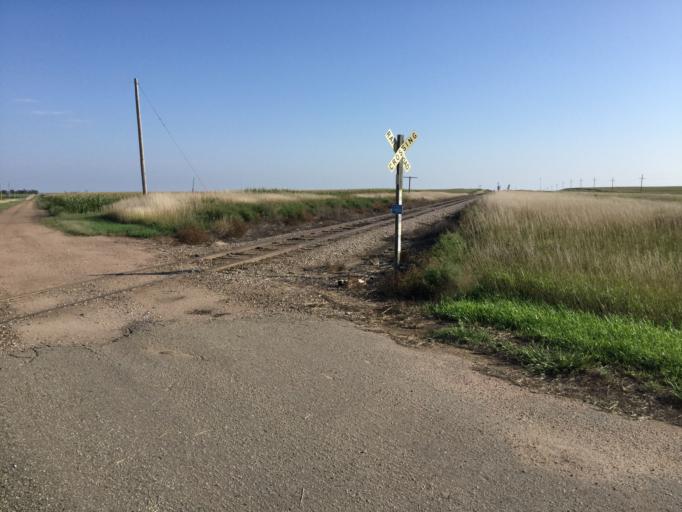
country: US
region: Kansas
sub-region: Decatur County
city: Oberlin
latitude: 39.6032
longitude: -100.4420
